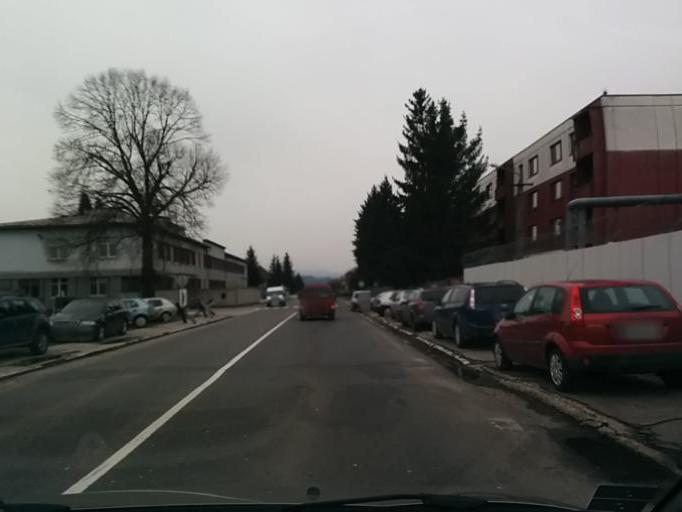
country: SK
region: Banskobystricky
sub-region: Okres Banska Bystrica
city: Zvolen
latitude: 48.6211
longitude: 19.1373
